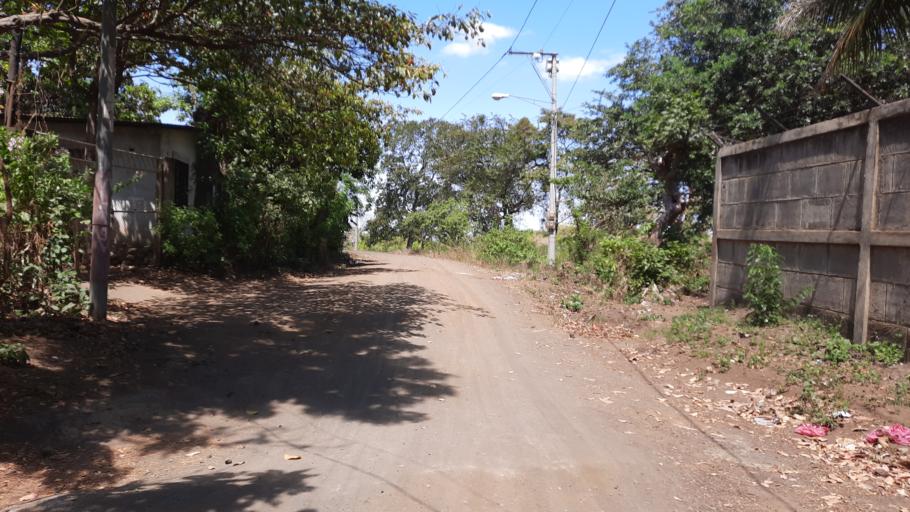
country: NI
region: Masaya
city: Ticuantepe
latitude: 12.0269
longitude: -86.1672
